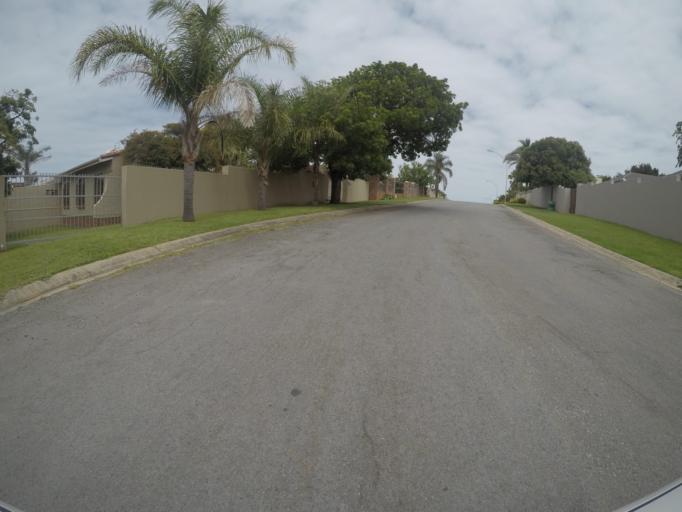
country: ZA
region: Eastern Cape
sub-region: Buffalo City Metropolitan Municipality
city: East London
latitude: -32.9788
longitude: 27.9518
